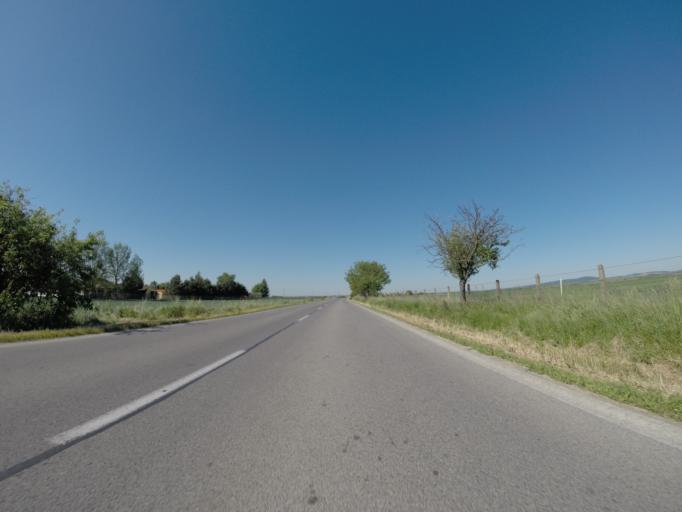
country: SK
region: Trnavsky
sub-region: Okres Trnava
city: Piestany
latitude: 48.5121
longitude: 17.9935
